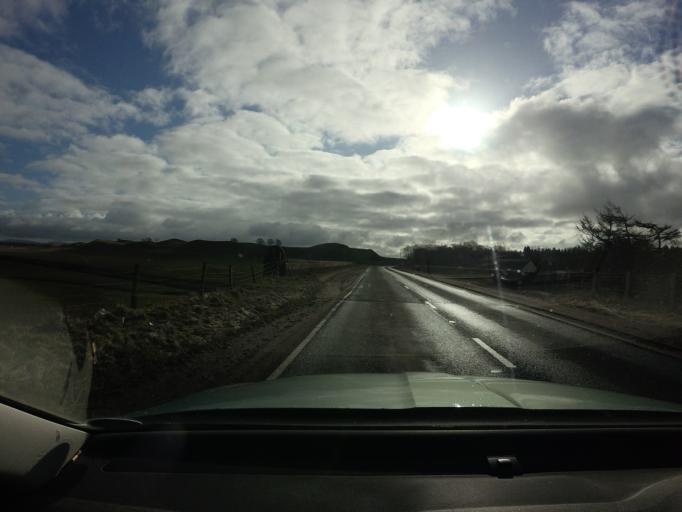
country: GB
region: Scotland
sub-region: South Lanarkshire
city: Forth
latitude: 55.7027
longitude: -3.6977
